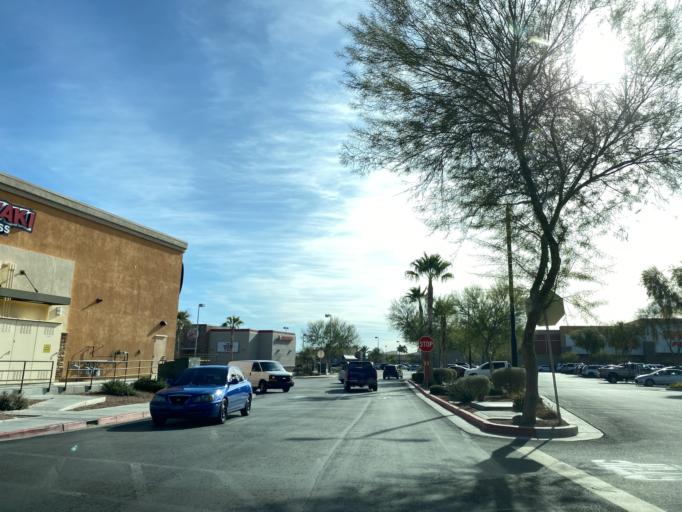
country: US
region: Nevada
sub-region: Clark County
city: North Las Vegas
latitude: 36.2713
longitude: -115.2077
